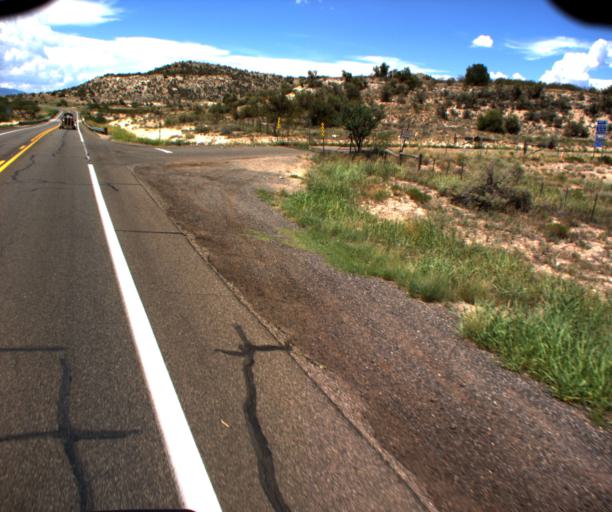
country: US
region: Arizona
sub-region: Yavapai County
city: Camp Verde
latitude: 34.5310
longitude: -111.8094
